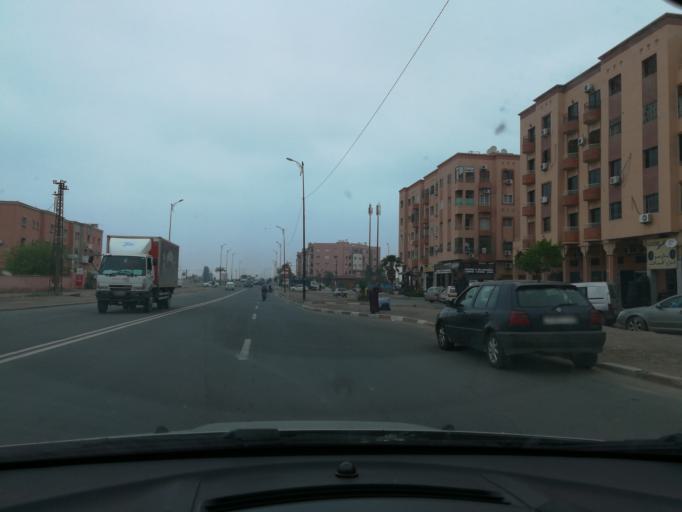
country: MA
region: Marrakech-Tensift-Al Haouz
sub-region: Marrakech
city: Marrakesh
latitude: 31.6635
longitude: -8.0312
